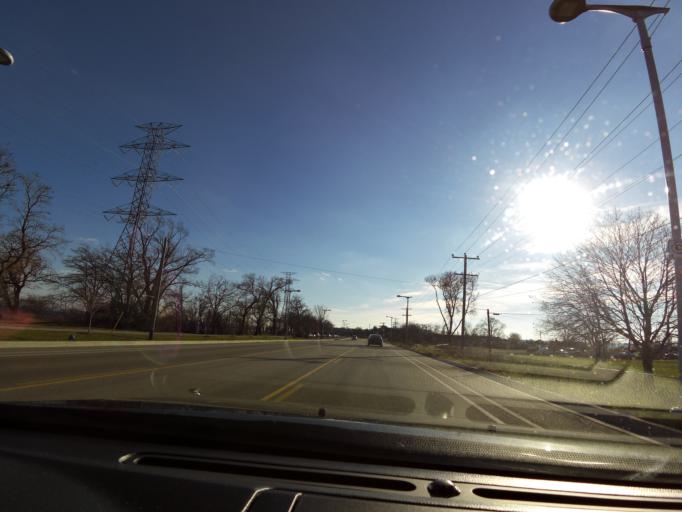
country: CA
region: Ontario
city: Burlington
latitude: 43.3145
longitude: -79.8011
